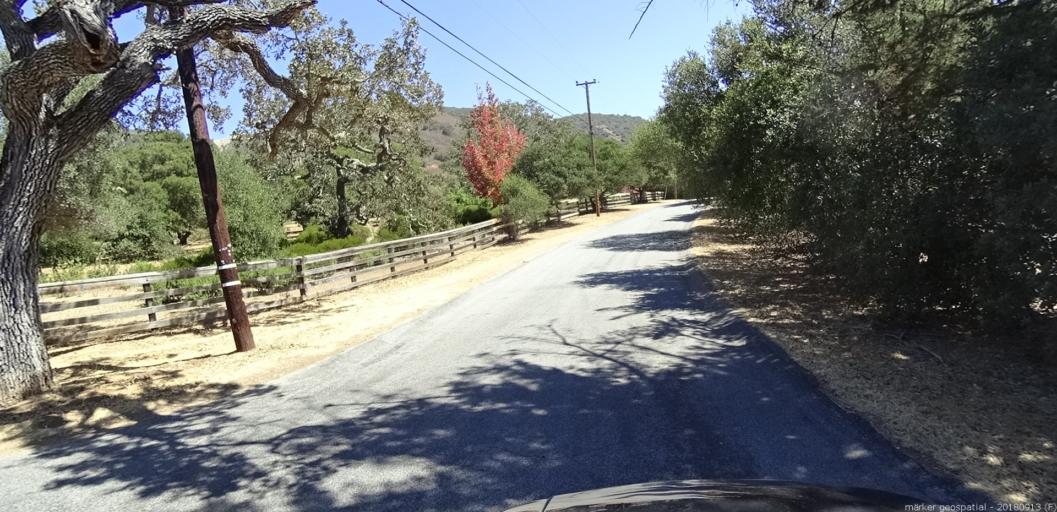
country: US
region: California
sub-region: Monterey County
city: Carmel Valley Village
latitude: 36.5086
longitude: -121.7563
